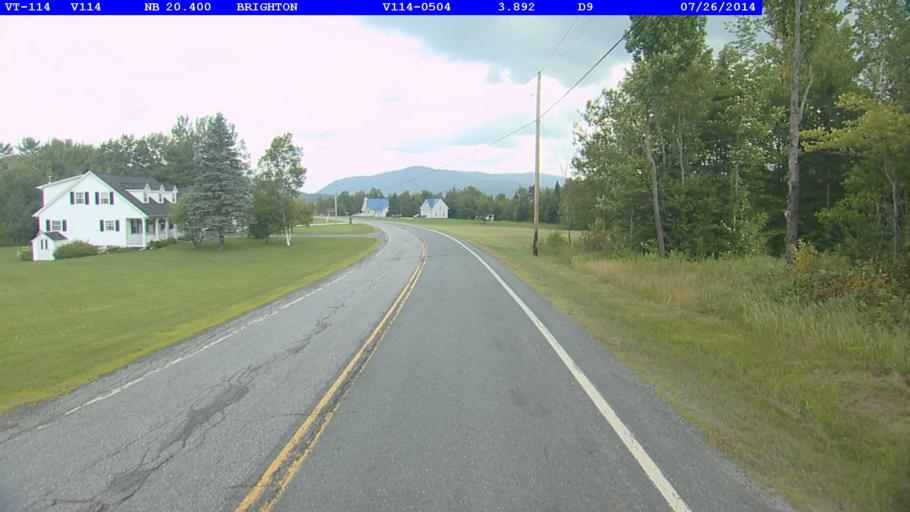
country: US
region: Vermont
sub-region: Caledonia County
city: Lyndonville
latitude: 44.7895
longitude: -71.9094
